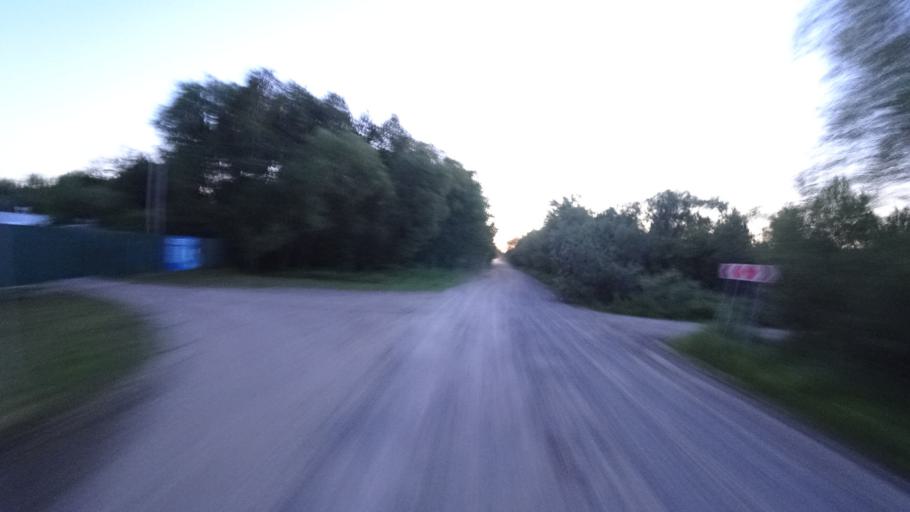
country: RU
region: Khabarovsk Krai
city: Khor
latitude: 47.8435
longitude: 134.9514
